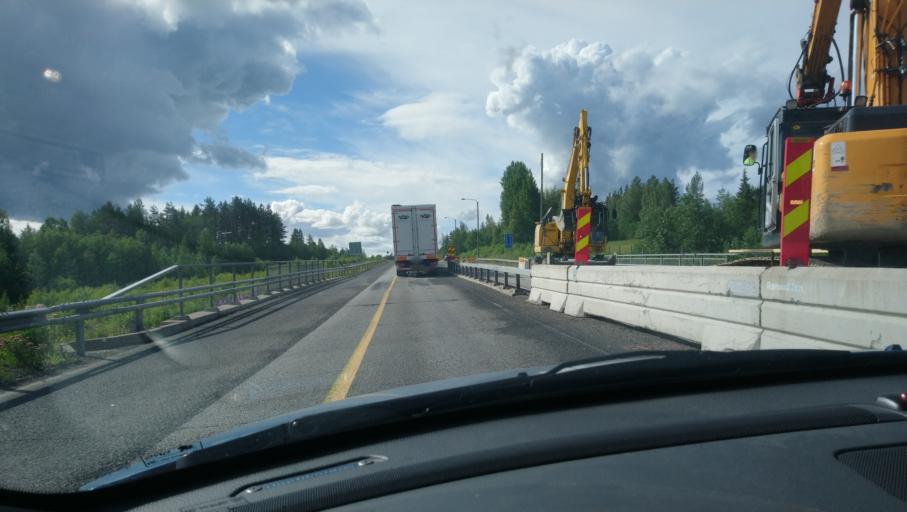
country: FI
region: Central Finland
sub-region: AEaenekoski
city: AEaenekoski
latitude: 62.5419
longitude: 25.6796
